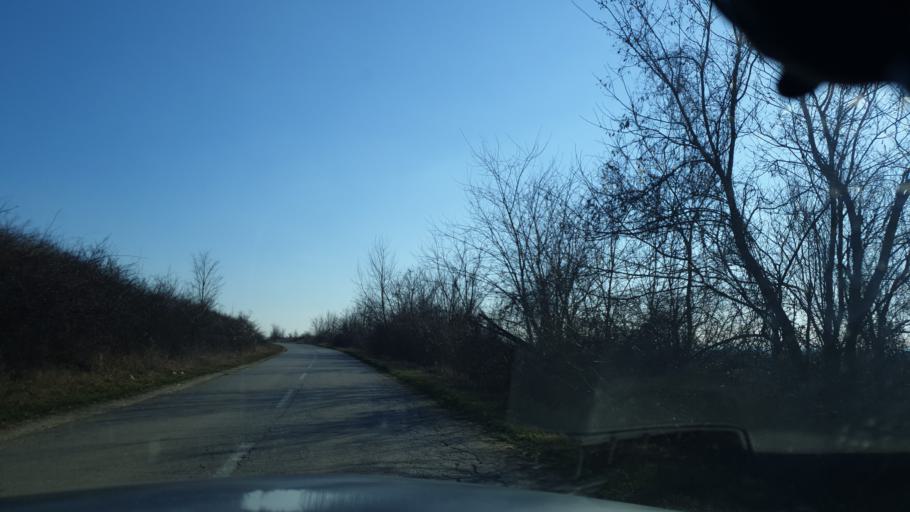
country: RS
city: Vrdnik
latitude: 45.0966
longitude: 19.8051
